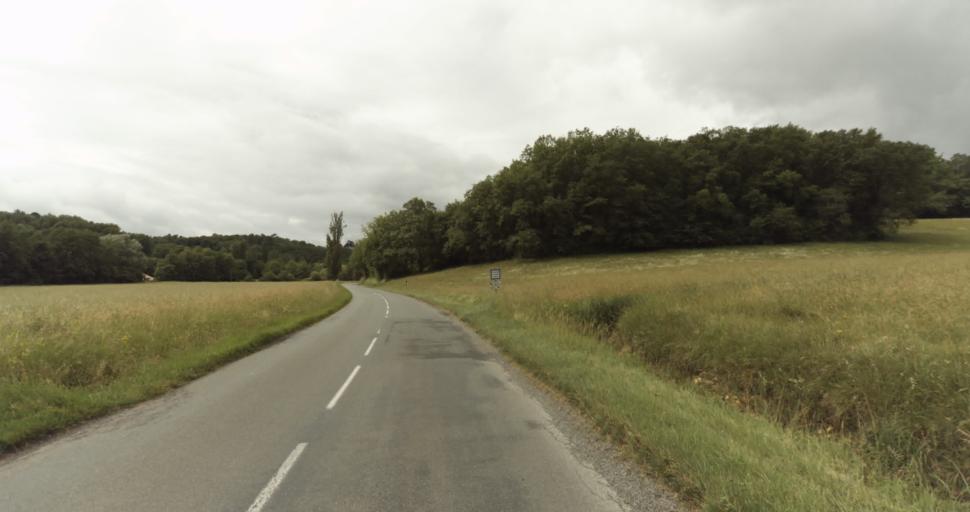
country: FR
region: Aquitaine
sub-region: Departement du Lot-et-Garonne
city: Villereal
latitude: 44.6737
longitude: 0.8880
